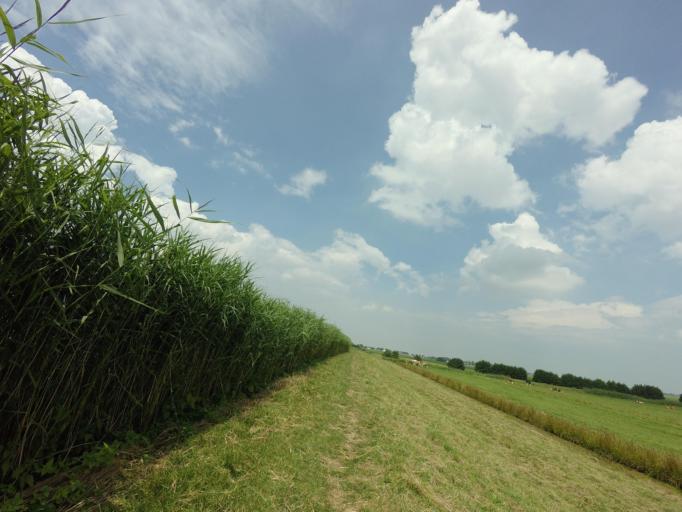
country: NL
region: South Holland
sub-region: Gemeente Vlist
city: Haastrecht
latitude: 52.0322
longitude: 4.8076
